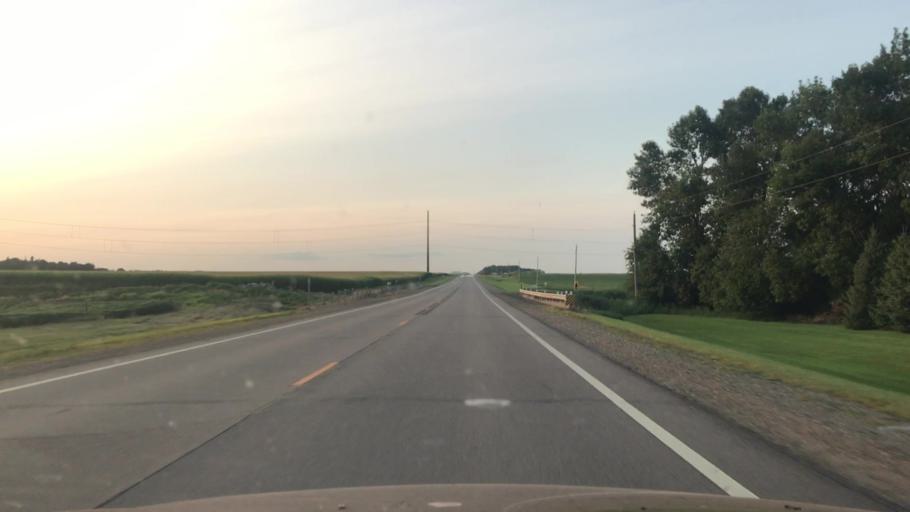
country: US
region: Minnesota
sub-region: Redwood County
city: Redwood Falls
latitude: 44.4294
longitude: -95.1176
